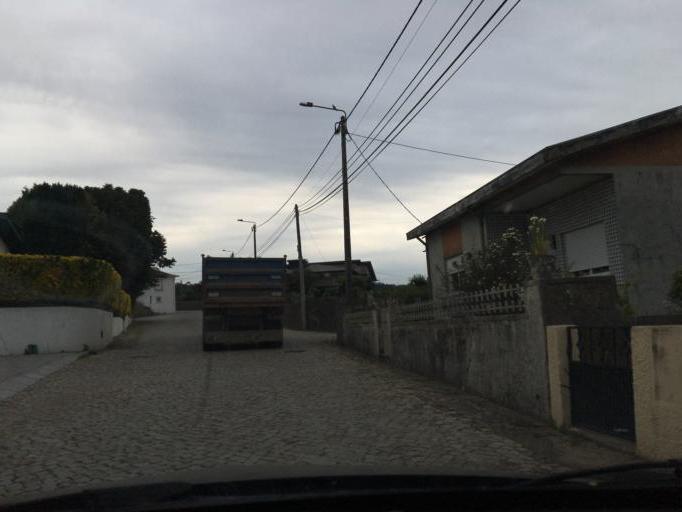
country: PT
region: Porto
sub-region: Maia
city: Anta
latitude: 41.2812
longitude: -8.6142
